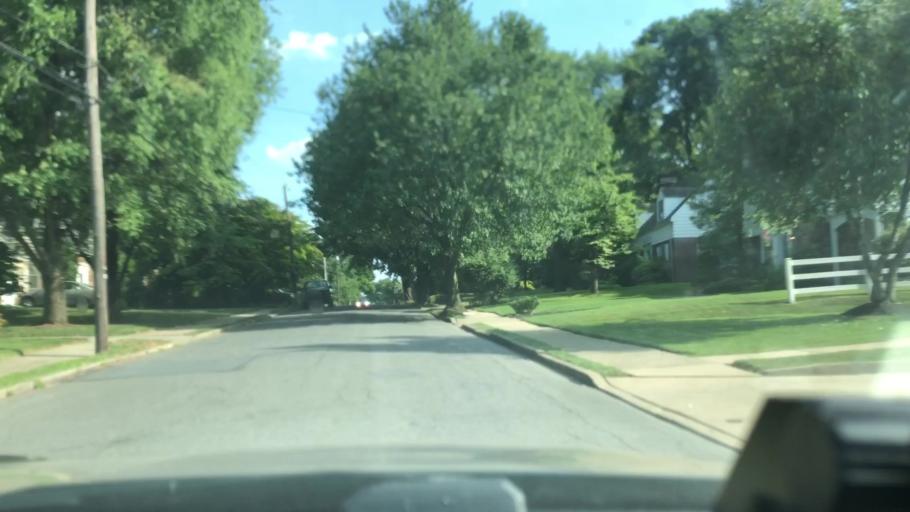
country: US
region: Pennsylvania
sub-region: Lehigh County
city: Fountain Hill
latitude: 40.6302
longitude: -75.4092
